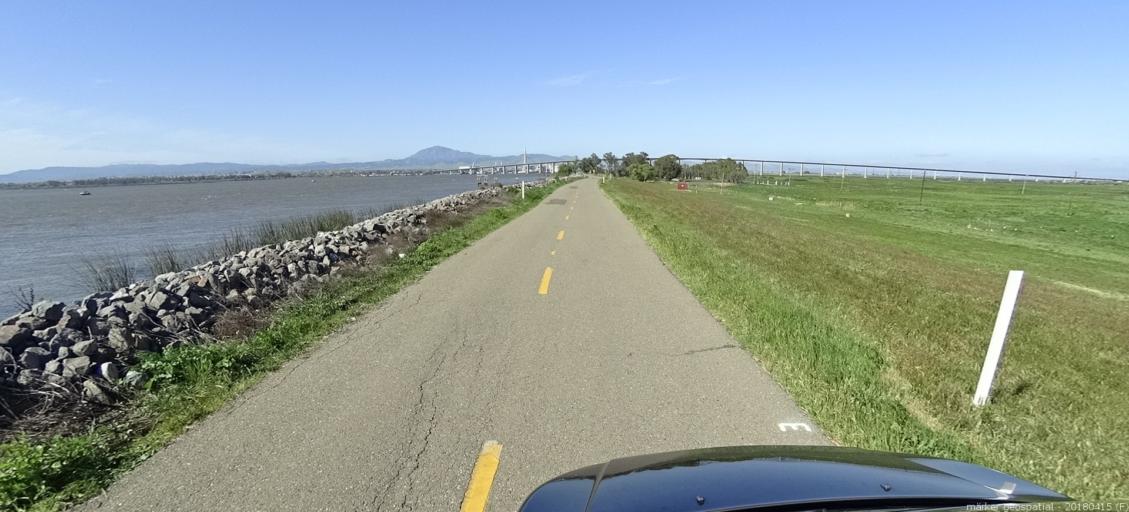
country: US
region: California
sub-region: Contra Costa County
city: Oakley
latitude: 38.0359
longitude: -121.7316
